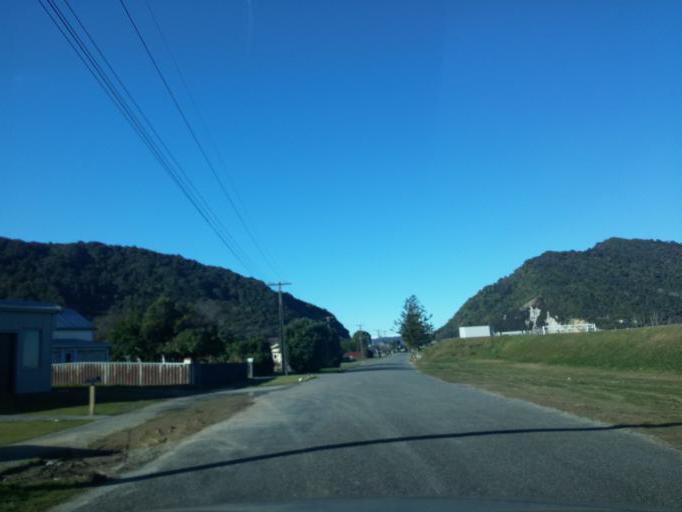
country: NZ
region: West Coast
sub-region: Grey District
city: Greymouth
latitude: -42.4418
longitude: 171.2080
